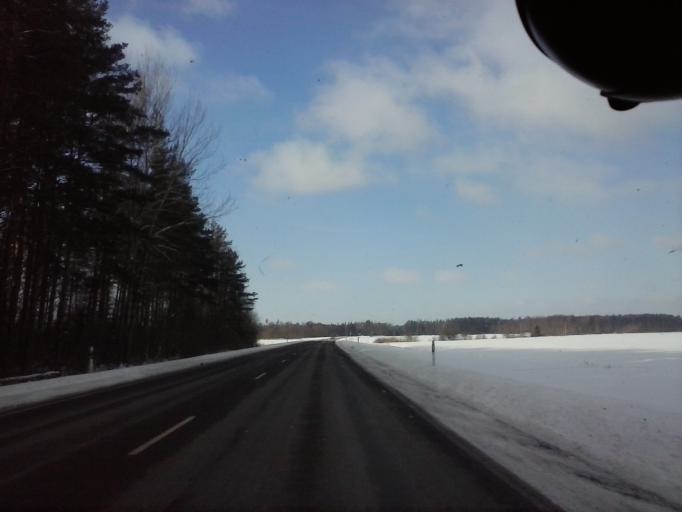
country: EE
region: Paernumaa
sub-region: Paikuse vald
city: Paikuse
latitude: 58.2709
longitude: 24.6354
